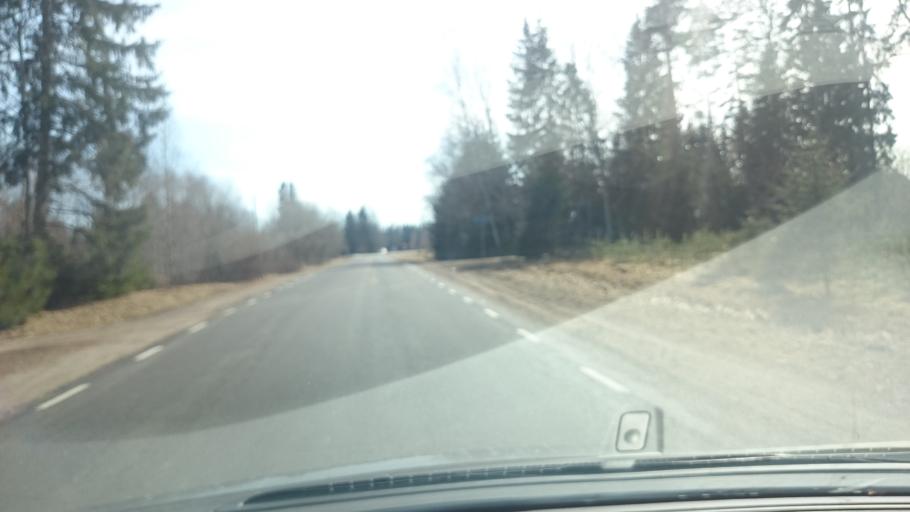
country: EE
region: Paernumaa
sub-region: Vaendra vald (alev)
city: Vandra
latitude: 58.6287
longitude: 24.9210
